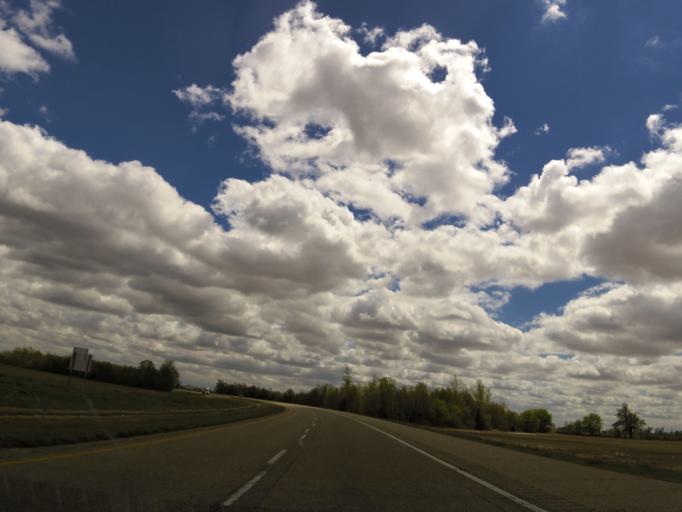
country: US
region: Arkansas
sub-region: Poinsett County
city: Trumann
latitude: 35.6620
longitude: -90.5501
